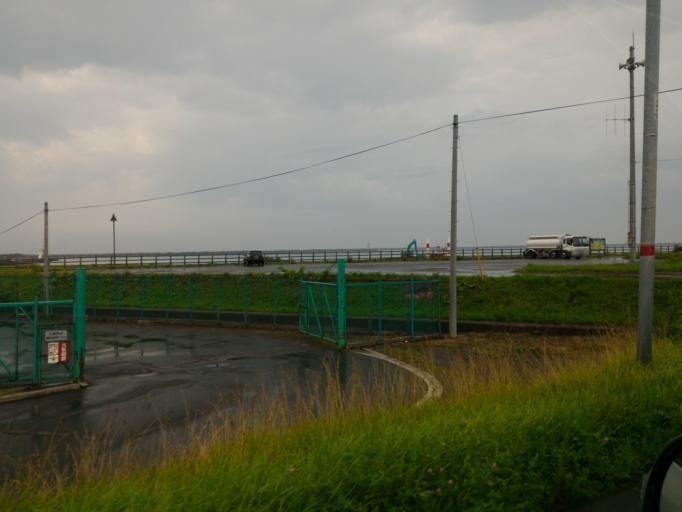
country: JP
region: Hokkaido
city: Rumoi
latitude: 43.9602
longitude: 141.6432
